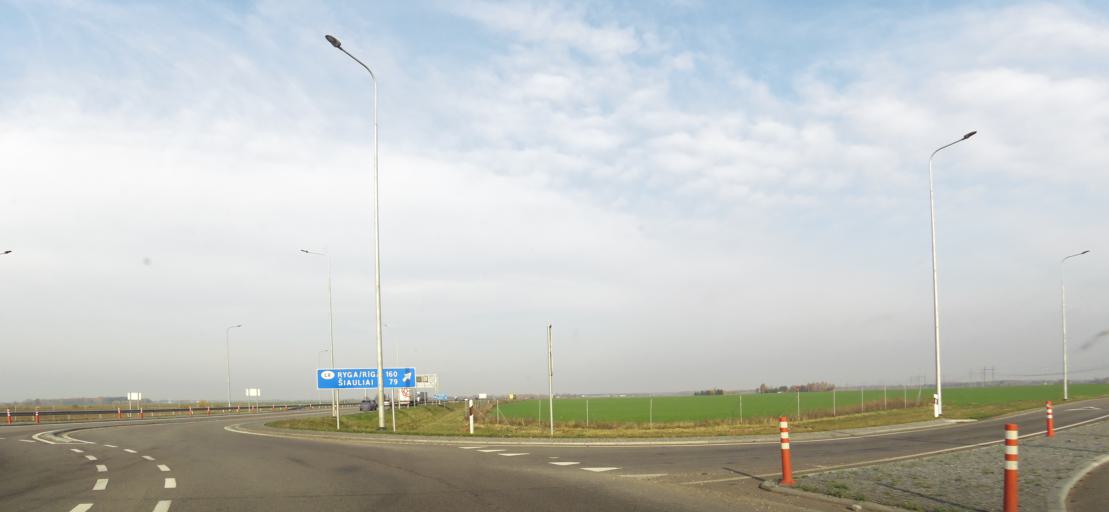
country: LT
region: Panevezys
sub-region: Panevezys City
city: Panevezys
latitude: 55.6902
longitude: 24.2787
